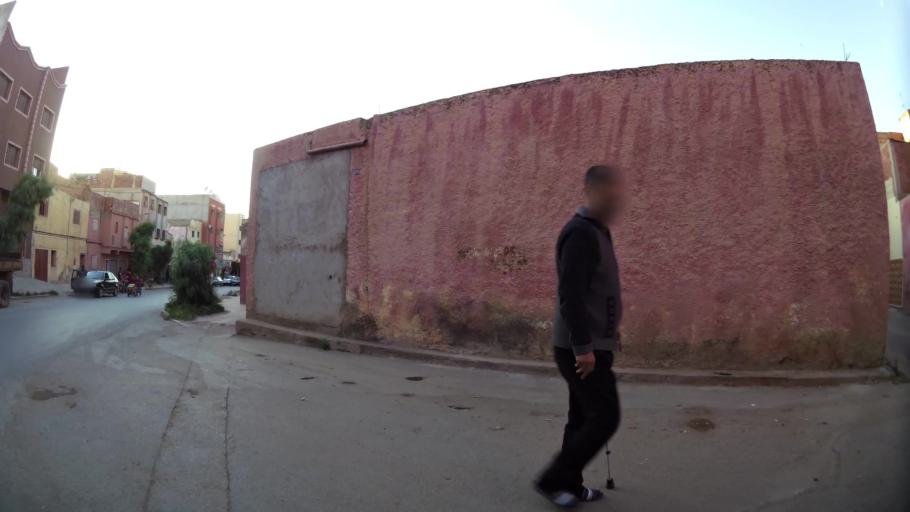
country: MA
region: Oriental
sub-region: Berkane-Taourirt
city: Berkane
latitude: 34.9194
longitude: -2.3289
